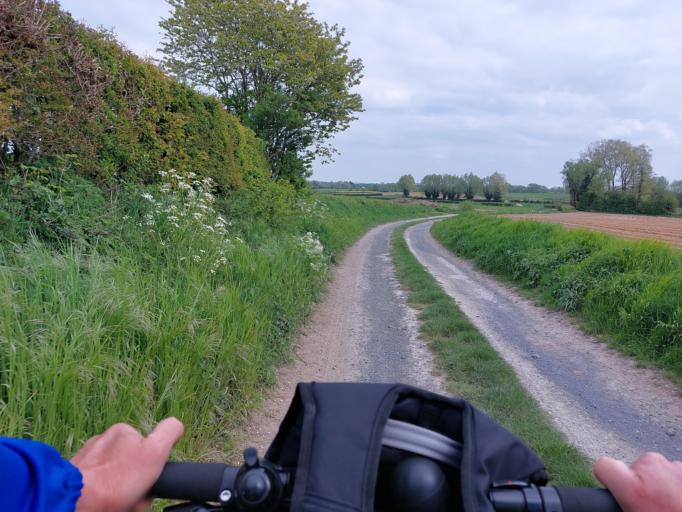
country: FR
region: Nord-Pas-de-Calais
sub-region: Departement du Nord
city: La Longueville
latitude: 50.2924
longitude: 3.8313
